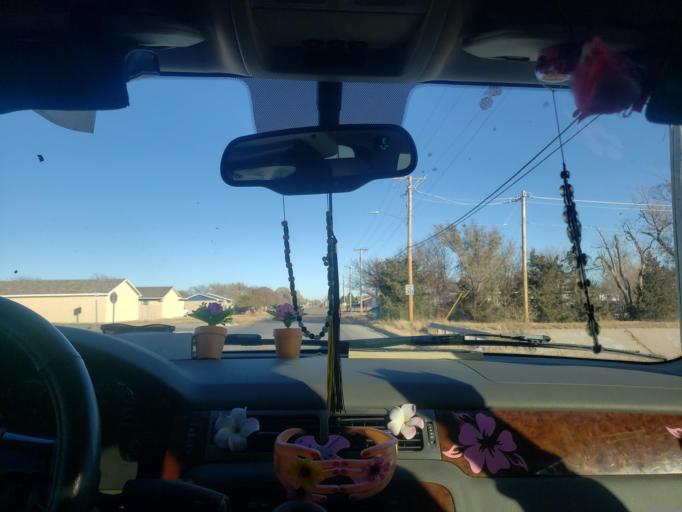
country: US
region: Kansas
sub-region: Finney County
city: Garden City
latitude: 37.9676
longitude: -100.8386
